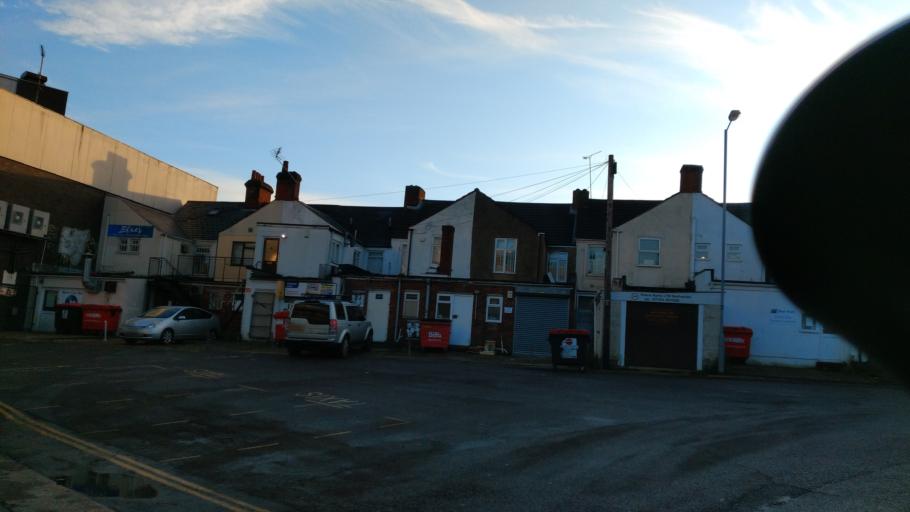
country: GB
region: England
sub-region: Borough of Swindon
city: Swindon
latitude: 51.5597
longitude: -1.7862
